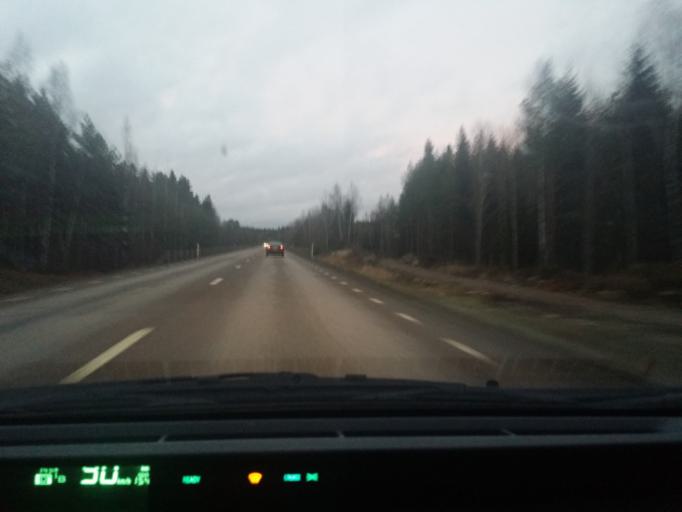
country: SE
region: Soedermanland
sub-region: Eskilstuna Kommun
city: Kvicksund
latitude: 59.5111
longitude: 16.3136
